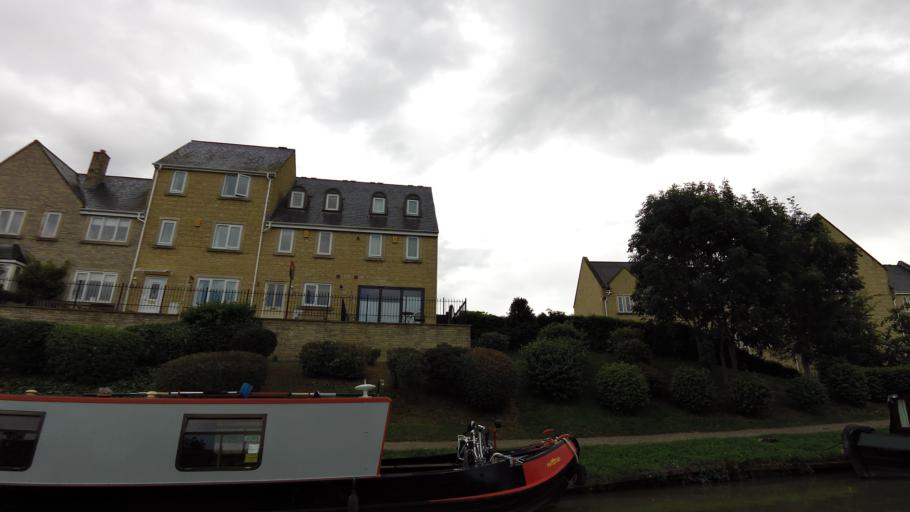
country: GB
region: England
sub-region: Wiltshire
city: Bradford-on-Avon
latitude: 51.3387
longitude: -2.2515
